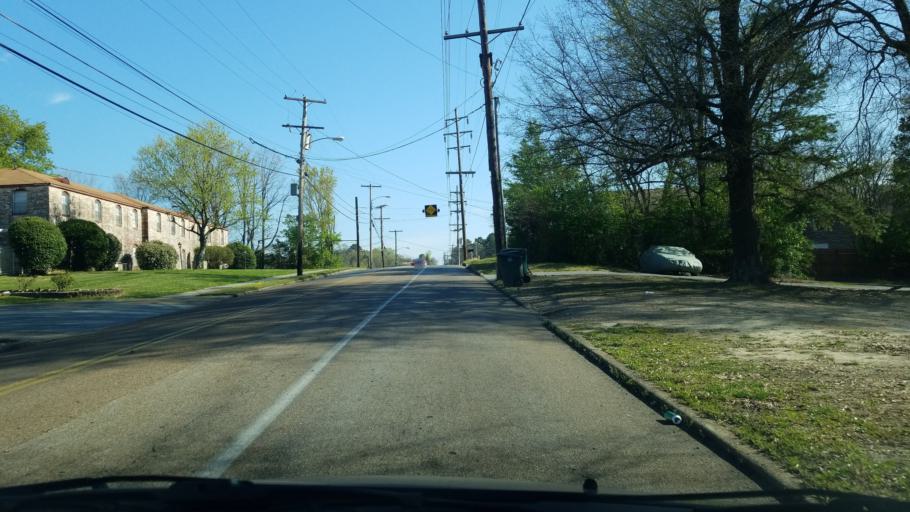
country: US
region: Tennessee
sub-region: Hamilton County
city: East Ridge
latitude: 35.0224
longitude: -85.2474
